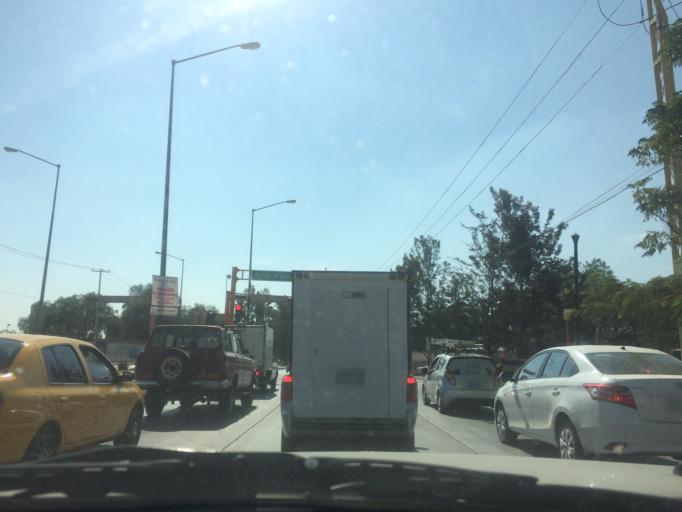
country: MX
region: Guanajuato
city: Leon
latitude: 21.1636
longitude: -101.6639
